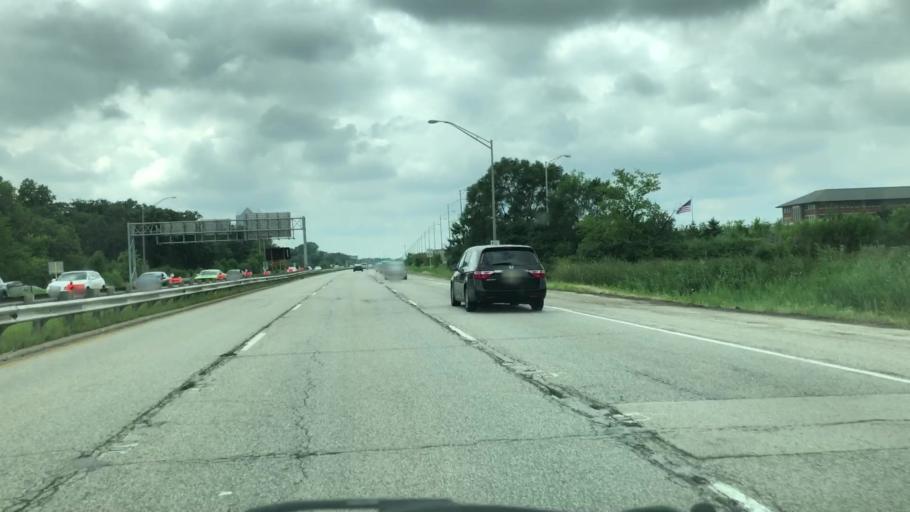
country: US
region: Illinois
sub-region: DuPage County
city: Oak Brook
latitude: 41.8616
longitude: -87.9326
